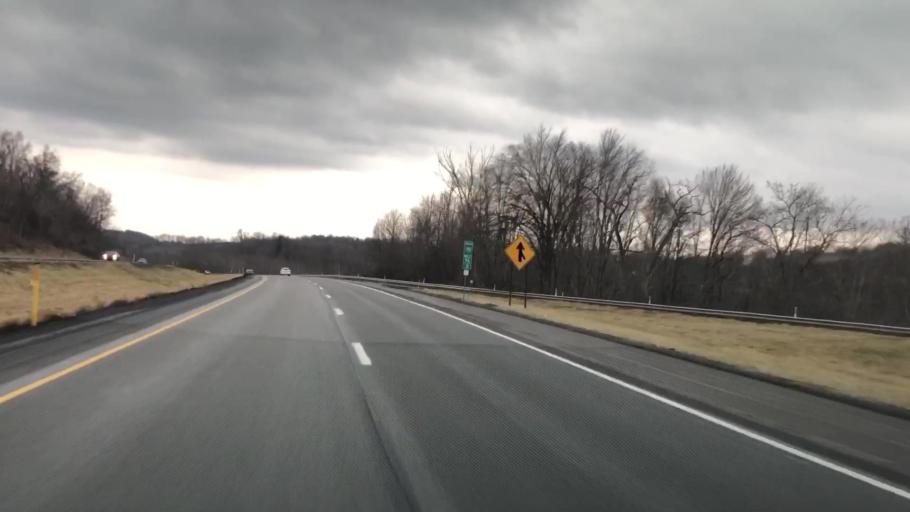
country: US
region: Pennsylvania
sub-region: Butler County
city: Prospect
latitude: 40.9203
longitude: -80.1333
